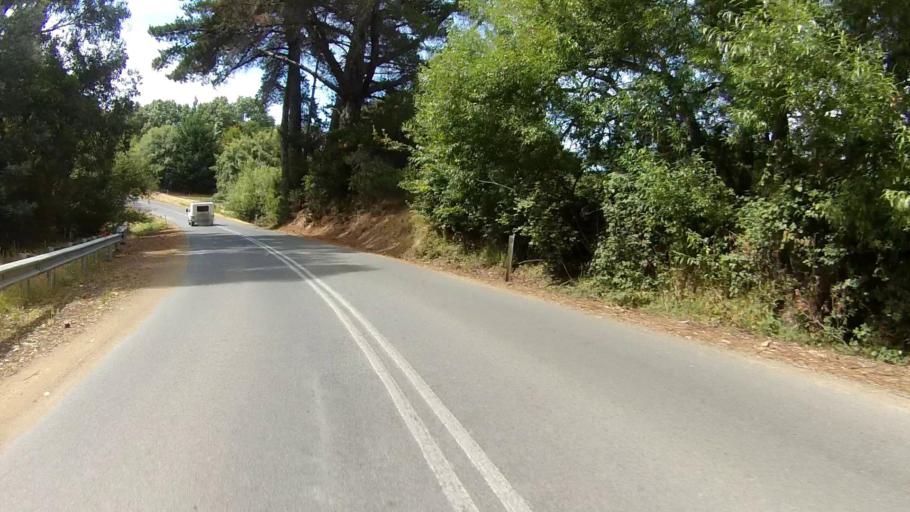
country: AU
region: Tasmania
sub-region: Kingborough
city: Kettering
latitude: -43.2059
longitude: 147.2529
